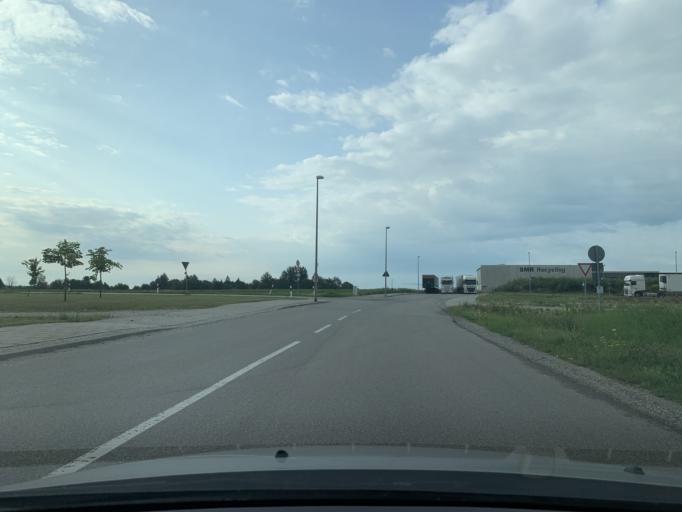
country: DE
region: Bavaria
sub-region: Upper Bavaria
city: Muehldorf
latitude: 48.2536
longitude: 12.5446
